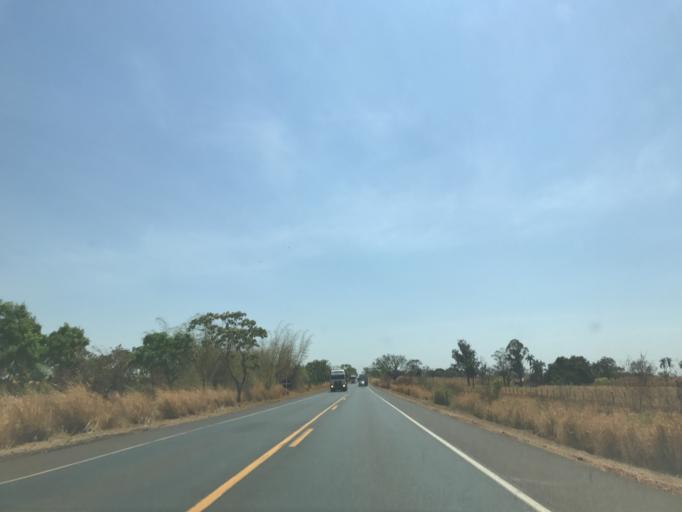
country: BR
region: Minas Gerais
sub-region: Frutal
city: Frutal
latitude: -20.0465
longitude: -49.0509
